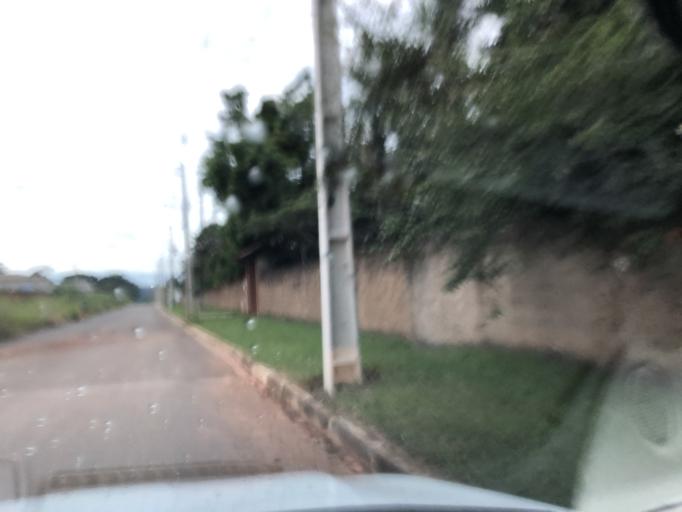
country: BR
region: Goias
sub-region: Luziania
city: Luziania
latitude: -16.1120
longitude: -47.9873
